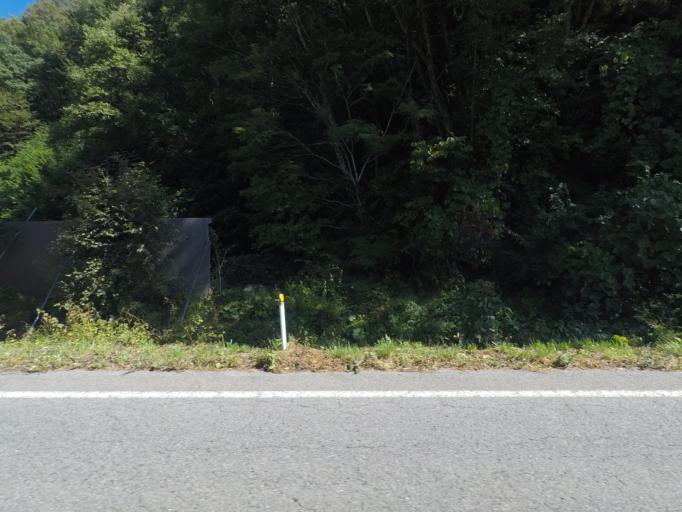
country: JP
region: Nagano
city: Tatsuno
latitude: 35.9783
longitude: 137.7478
